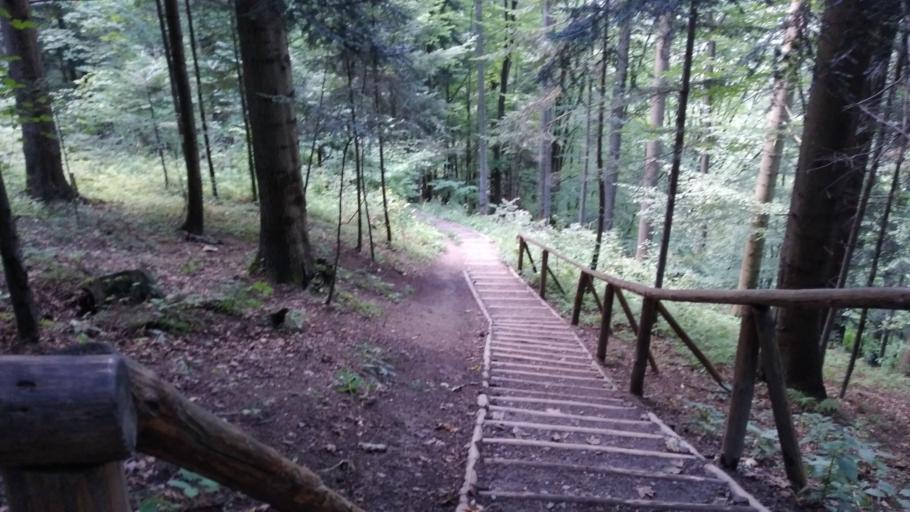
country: PL
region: Lesser Poland Voivodeship
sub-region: Powiat nowotarski
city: Kroscienko nad Dunajcem
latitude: 49.4211
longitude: 20.4440
